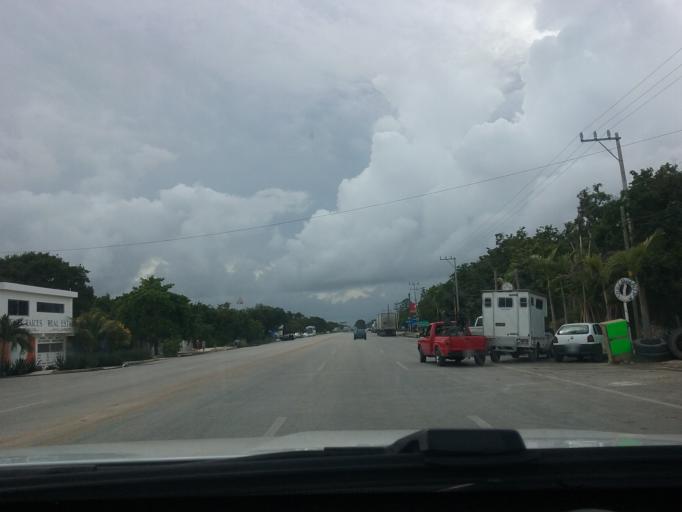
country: MX
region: Quintana Roo
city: Tulum
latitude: 20.2080
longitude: -87.4730
